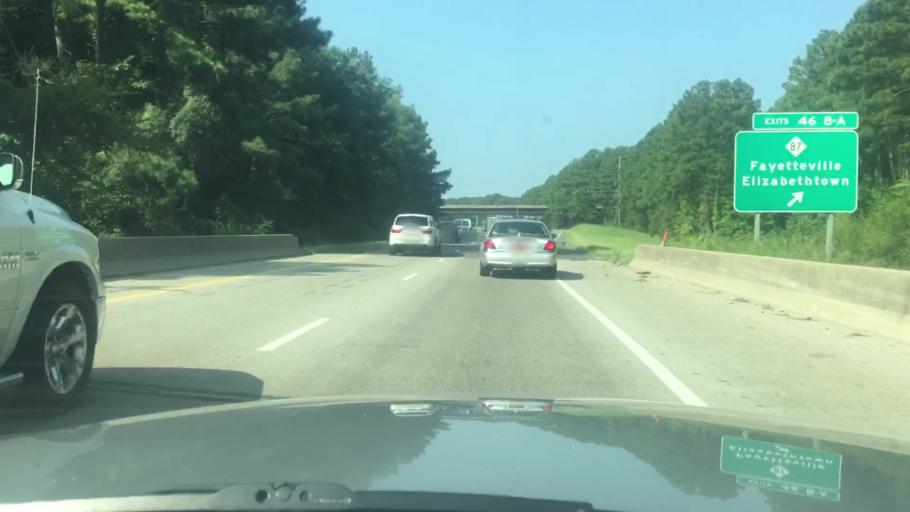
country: US
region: North Carolina
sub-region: Cumberland County
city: Vander
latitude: 34.9821
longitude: -78.8486
